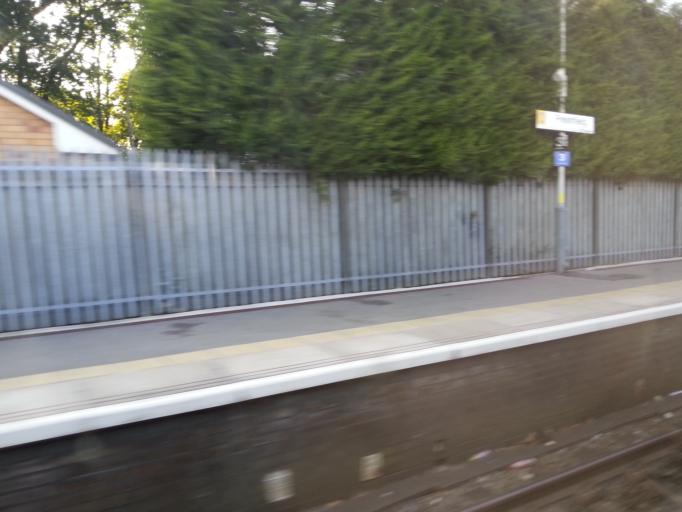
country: GB
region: England
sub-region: Sefton
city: Formby
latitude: 53.5667
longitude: -3.0719
